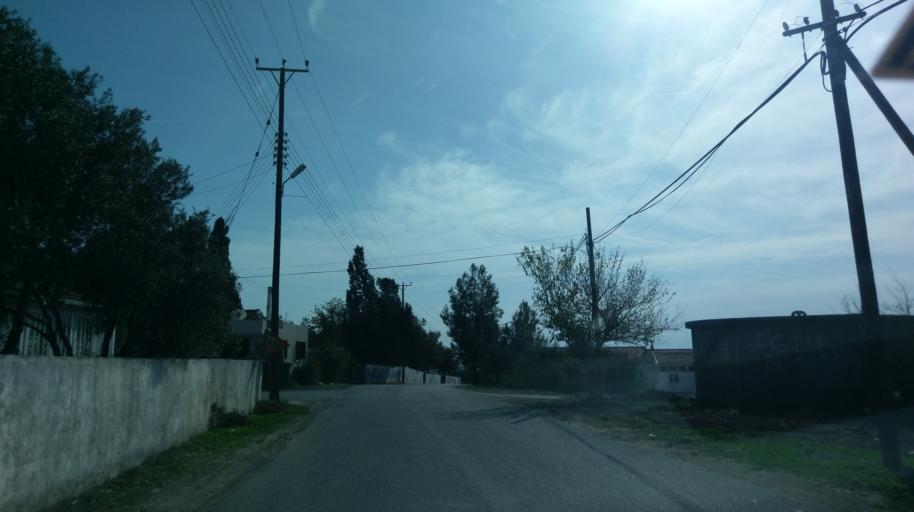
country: CY
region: Keryneia
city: Lapithos
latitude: 35.2672
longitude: 33.2245
